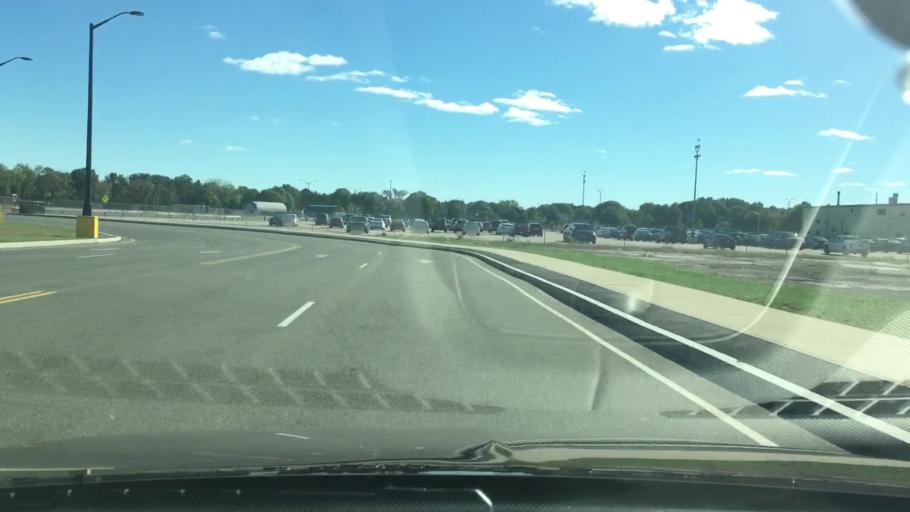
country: US
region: Connecticut
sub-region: Hartford County
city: East Hartford
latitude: 41.7485
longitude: -72.6301
